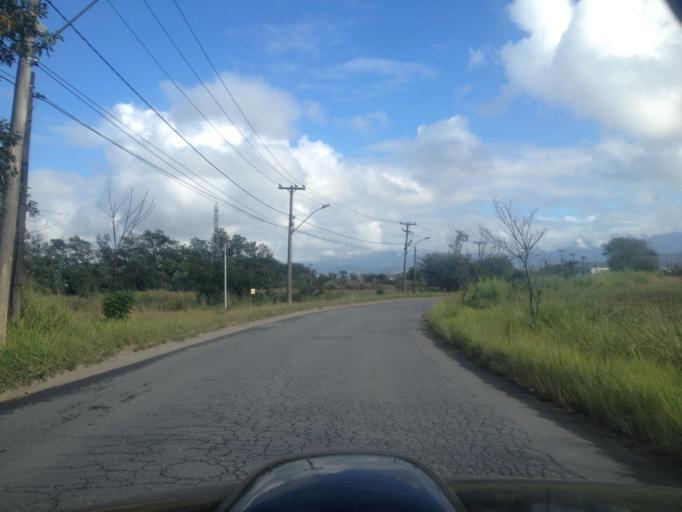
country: BR
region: Rio de Janeiro
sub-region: Resende
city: Resende
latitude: -22.4530
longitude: -44.3749
